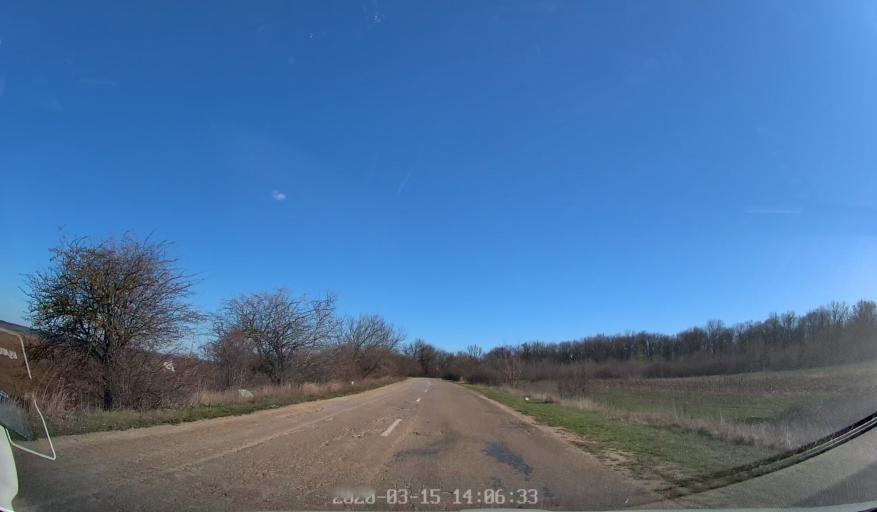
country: MD
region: Orhei
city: Orhei
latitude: 47.3040
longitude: 28.9463
